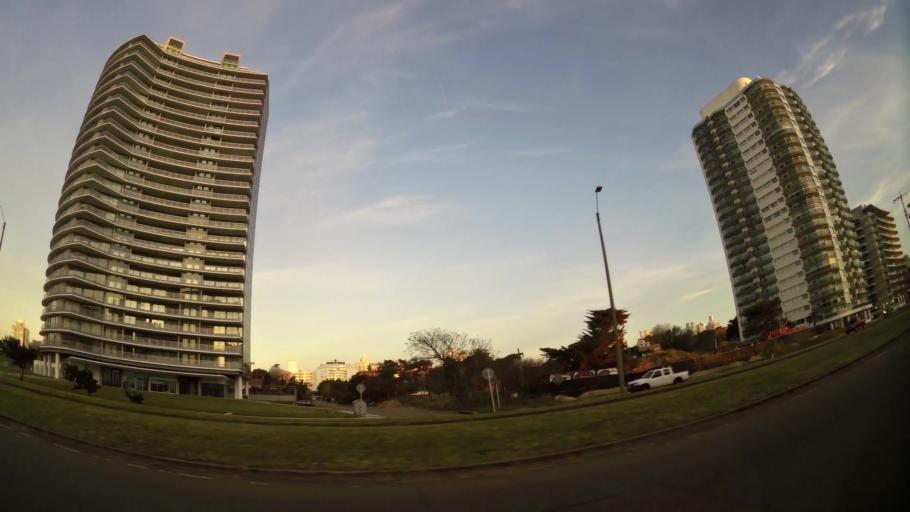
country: UY
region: Maldonado
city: Punta del Este
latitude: -34.9484
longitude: -54.9373
